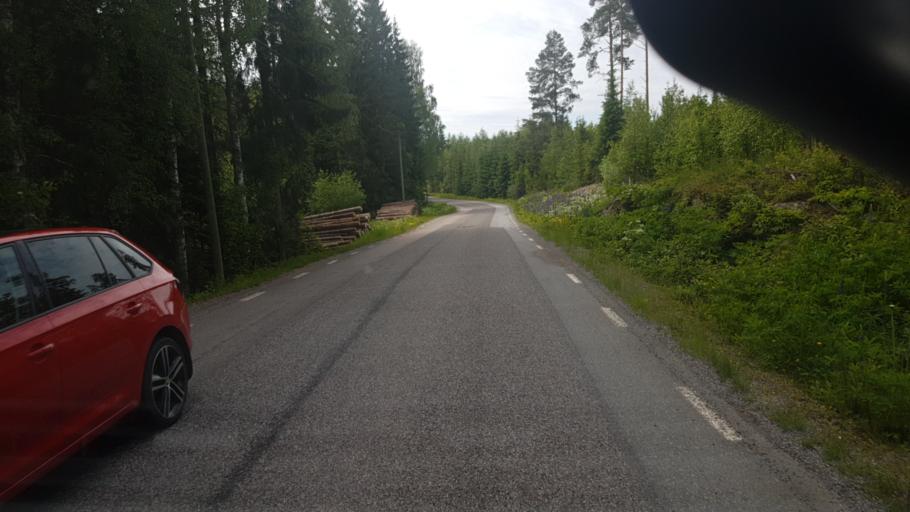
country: SE
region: Vaermland
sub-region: Eda Kommun
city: Charlottenberg
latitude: 59.8817
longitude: 12.3547
